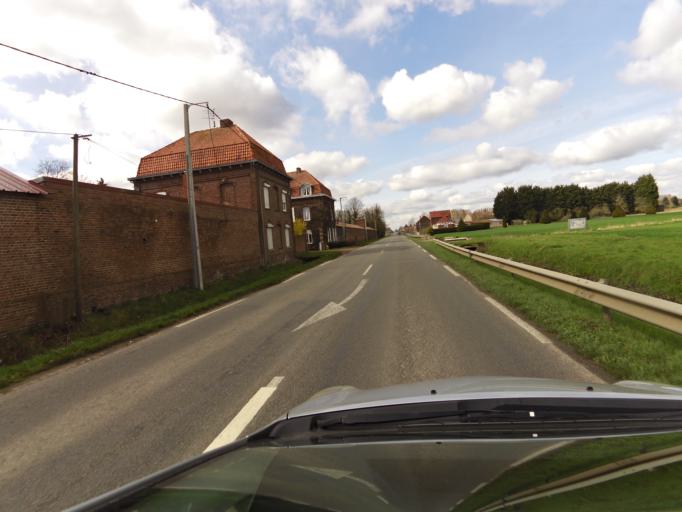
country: FR
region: Nord-Pas-de-Calais
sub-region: Departement du Pas-de-Calais
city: Lorgies
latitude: 50.5625
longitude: 2.7848
